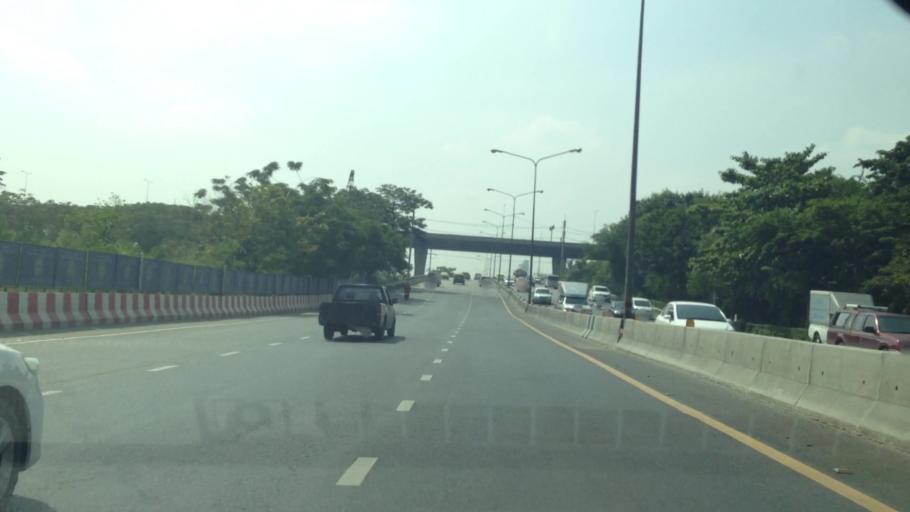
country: TH
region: Bangkok
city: Bang Na
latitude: 13.6684
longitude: 100.6449
